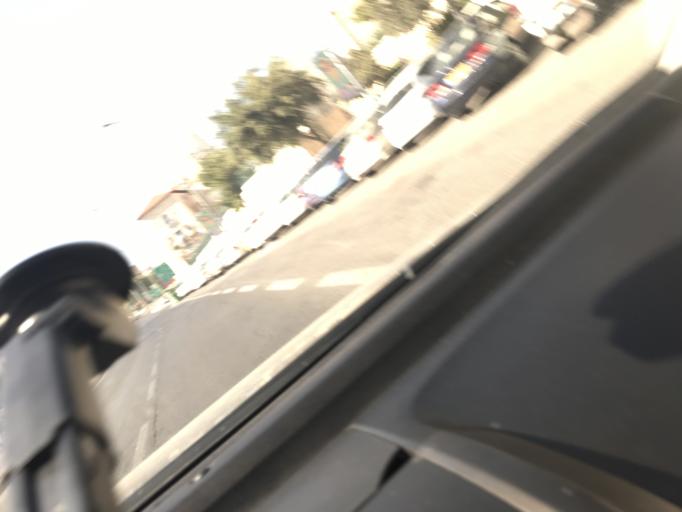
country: IL
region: Jerusalem
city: West Jerusalem
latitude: 31.7812
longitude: 35.2087
